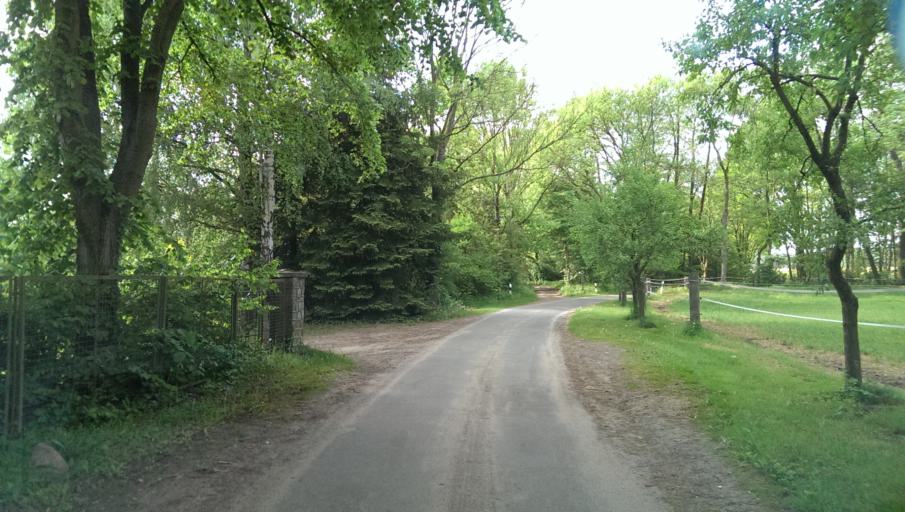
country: DE
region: Brandenburg
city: Linthe
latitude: 52.1510
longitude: 12.7201
